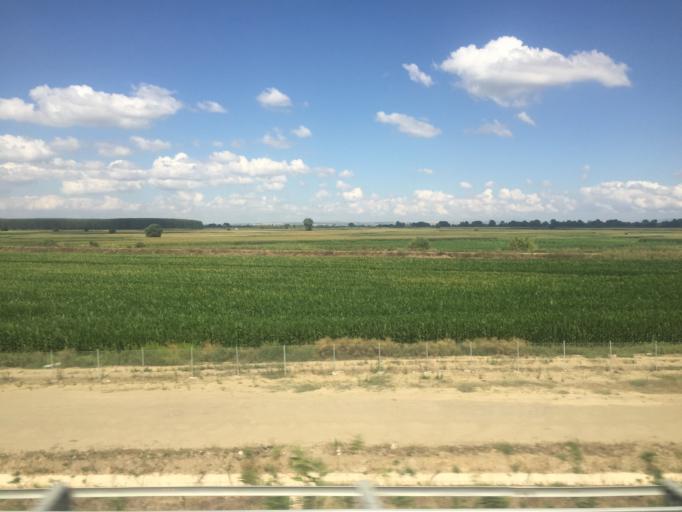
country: TR
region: Bursa
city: Tatkavakli
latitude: 40.0933
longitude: 28.2755
